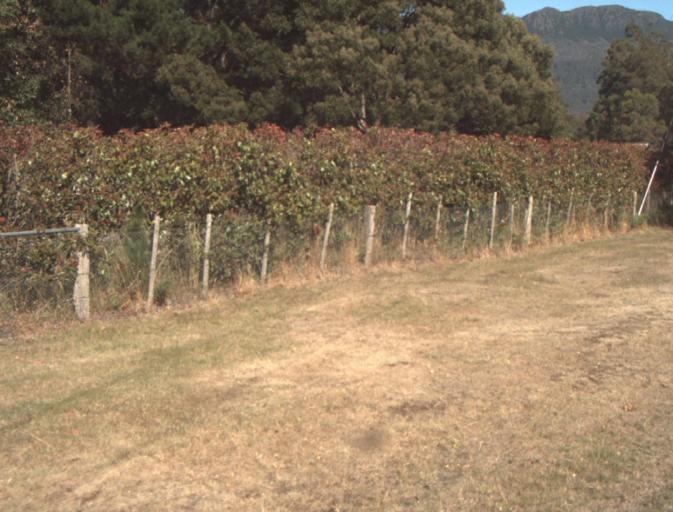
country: AU
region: Tasmania
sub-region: Dorset
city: Scottsdale
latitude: -41.2956
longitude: 147.3526
